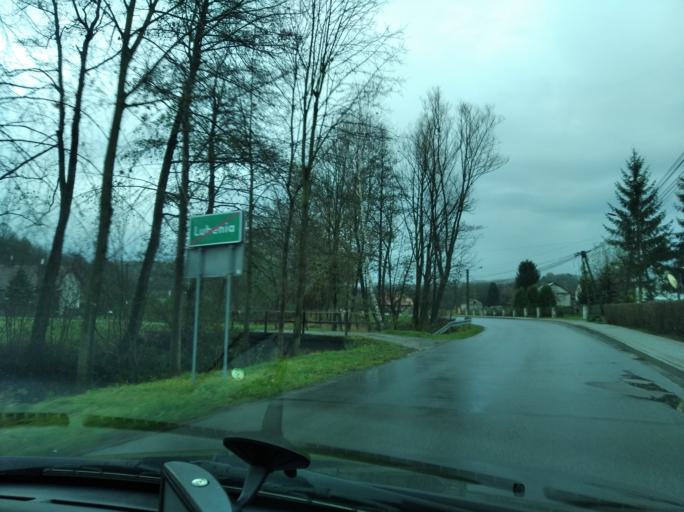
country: PL
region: Subcarpathian Voivodeship
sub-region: Powiat rzeszowski
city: Straszydle
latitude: 49.9154
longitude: 21.9579
